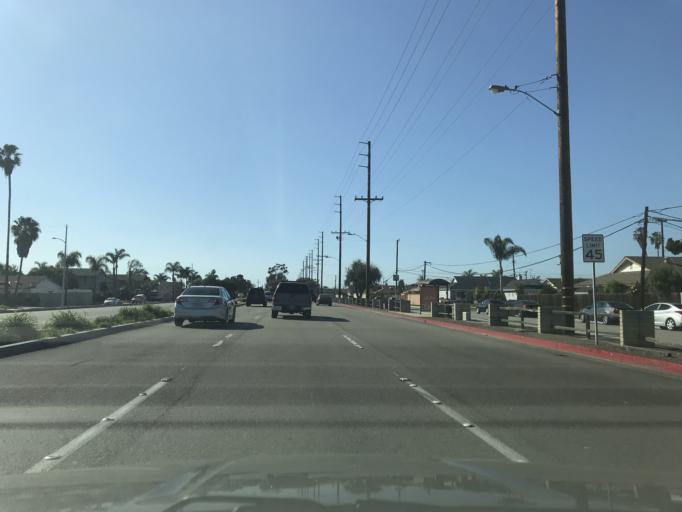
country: US
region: California
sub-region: Orange County
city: Fountain Valley
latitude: 33.6724
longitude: -117.9627
